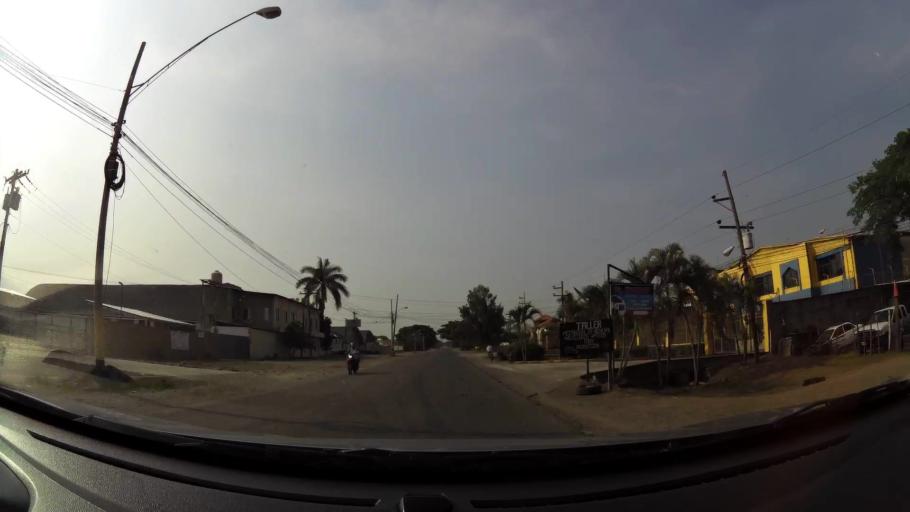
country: HN
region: Comayagua
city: Comayagua
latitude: 14.4354
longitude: -87.6333
